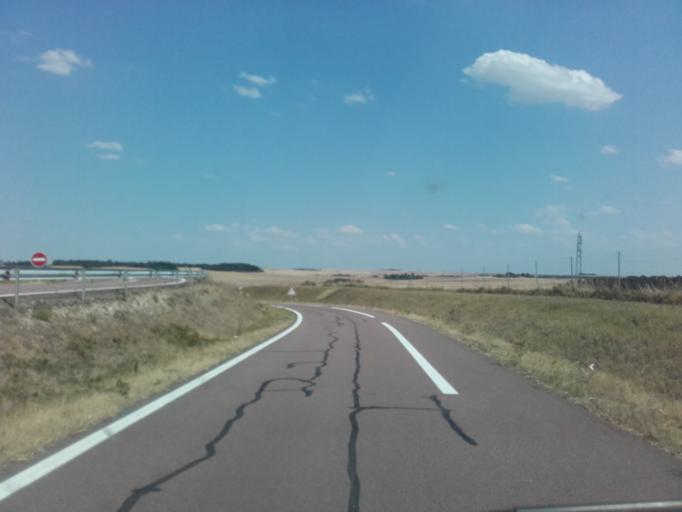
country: FR
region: Bourgogne
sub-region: Departement de l'Yonne
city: Joux-la-Ville
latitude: 47.6591
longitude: 3.8820
